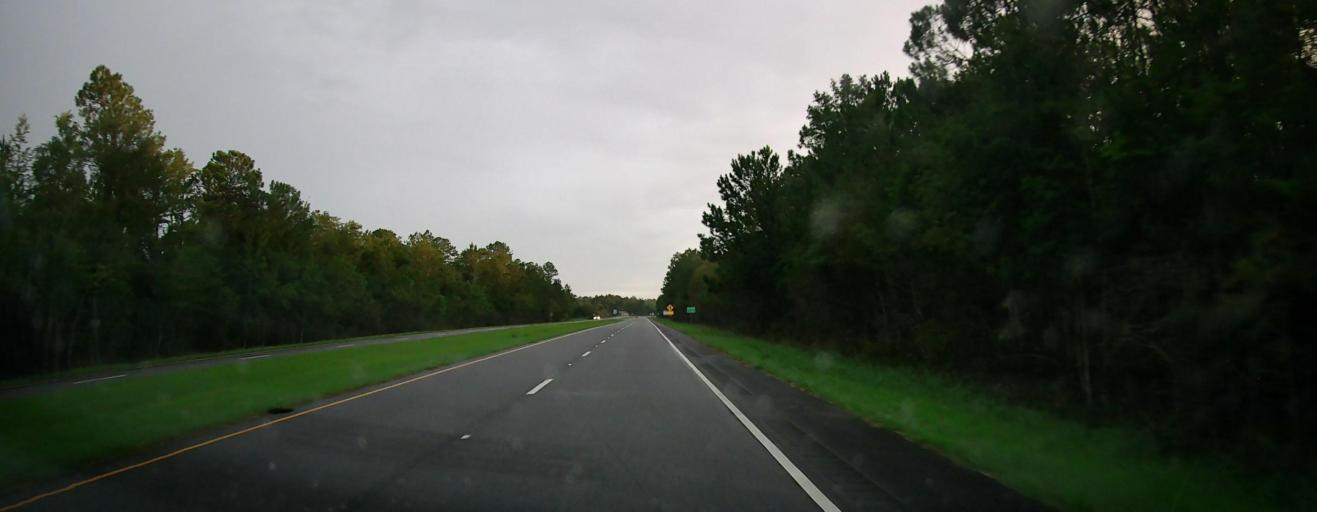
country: US
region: Georgia
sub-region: Clinch County
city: Homerville
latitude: 30.9968
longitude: -82.8648
